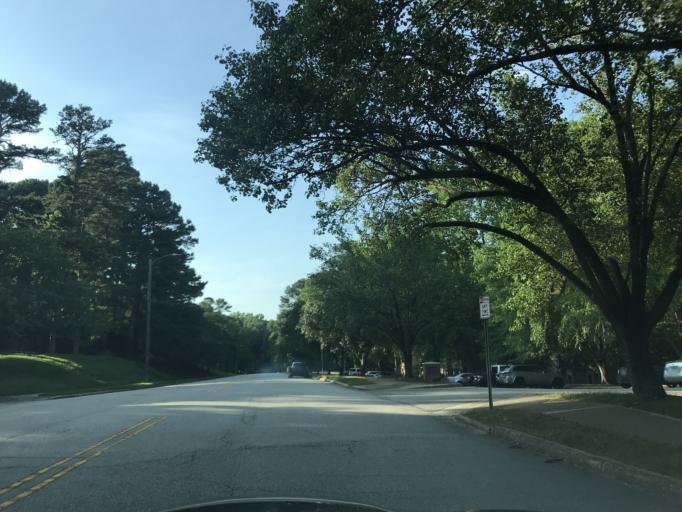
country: US
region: North Carolina
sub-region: Wake County
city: West Raleigh
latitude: 35.8220
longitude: -78.6902
